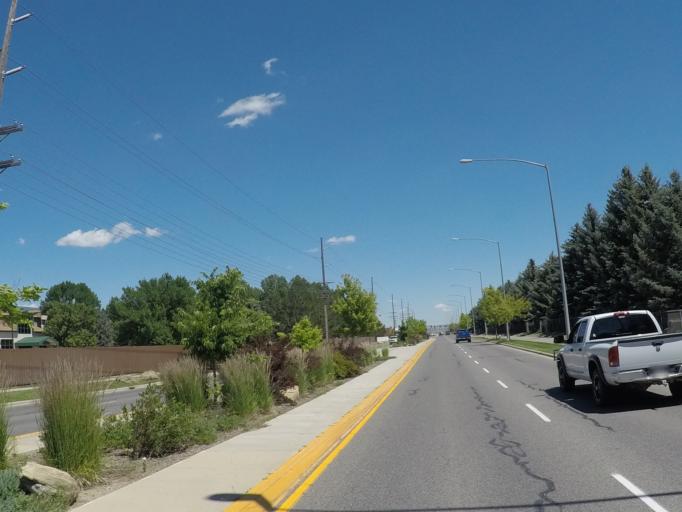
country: US
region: Montana
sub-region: Yellowstone County
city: Billings
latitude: 45.7551
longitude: -108.6019
